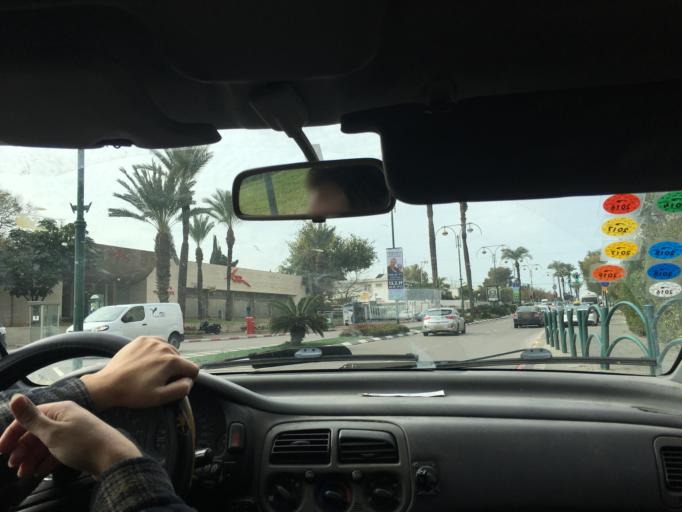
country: IL
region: Tel Aviv
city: Ramat HaSharon
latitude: 32.1371
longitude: 34.8426
